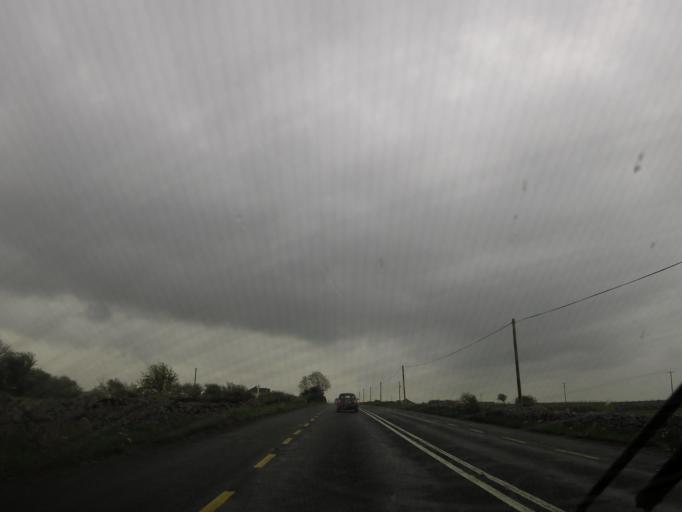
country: IE
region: Connaught
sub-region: County Galway
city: Tuam
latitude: 53.4781
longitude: -8.9091
